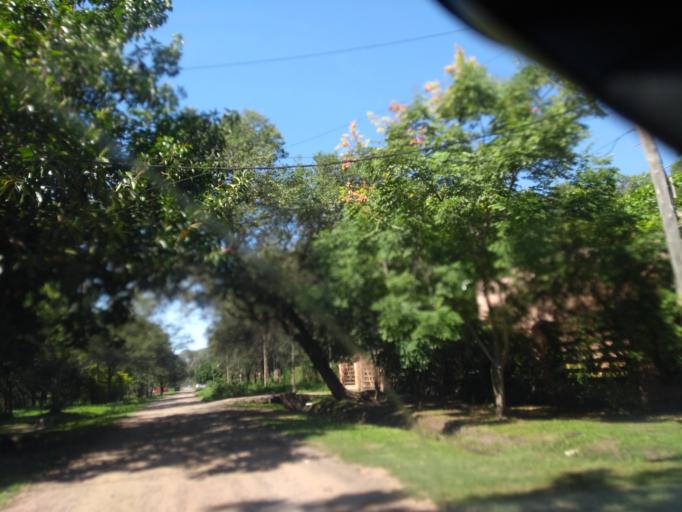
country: AR
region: Chaco
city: Resistencia
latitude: -27.4289
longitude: -58.9457
